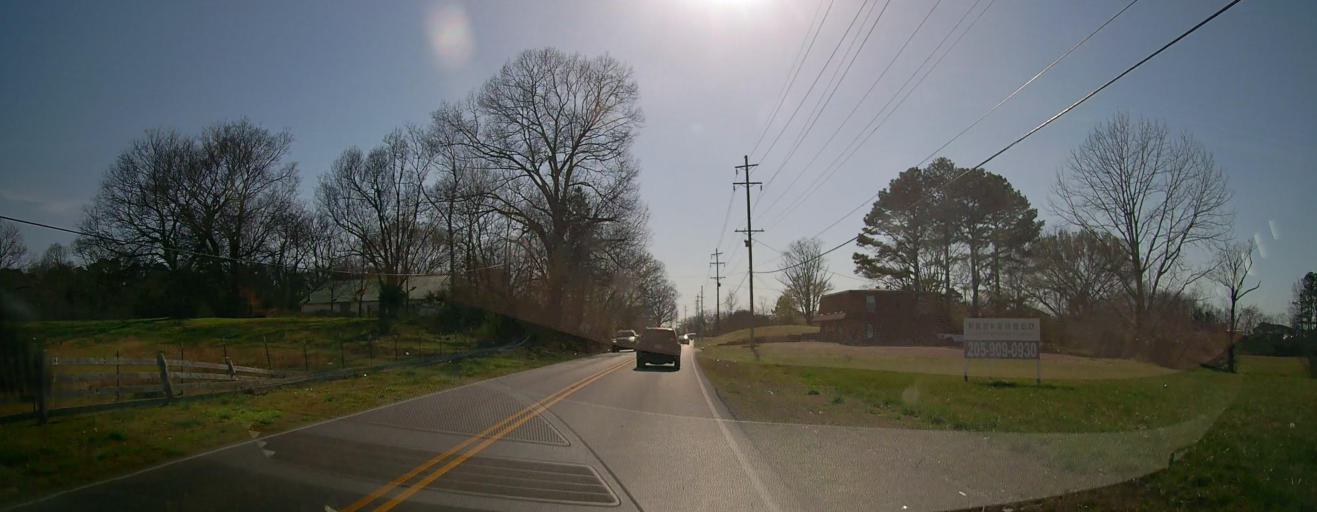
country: US
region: Alabama
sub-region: Lauderdale County
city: East Florence
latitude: 34.8304
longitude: -87.6158
